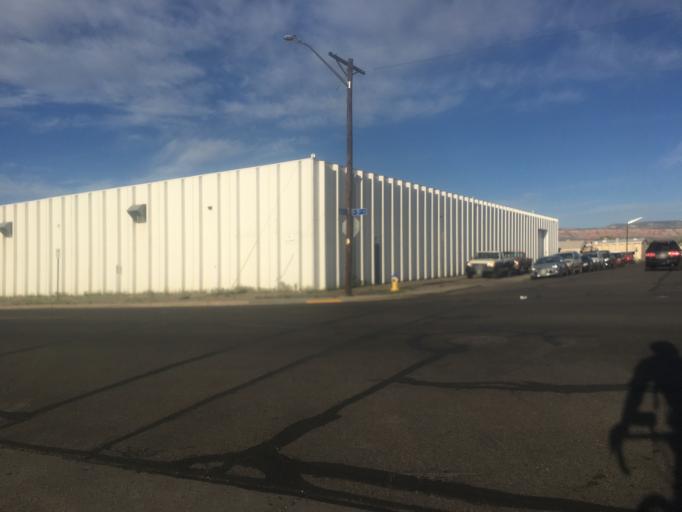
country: US
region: Colorado
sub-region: Mesa County
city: Grand Junction
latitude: 39.0790
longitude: -108.5644
